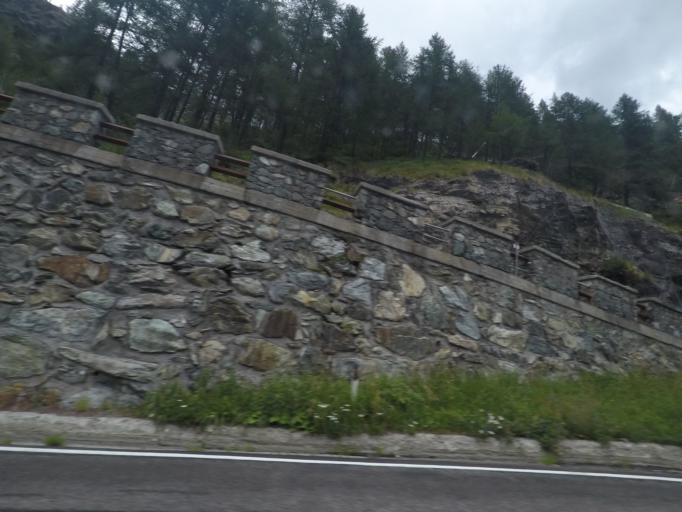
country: IT
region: Aosta Valley
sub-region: Valle d'Aosta
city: Paquier
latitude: 45.9032
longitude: 7.6185
